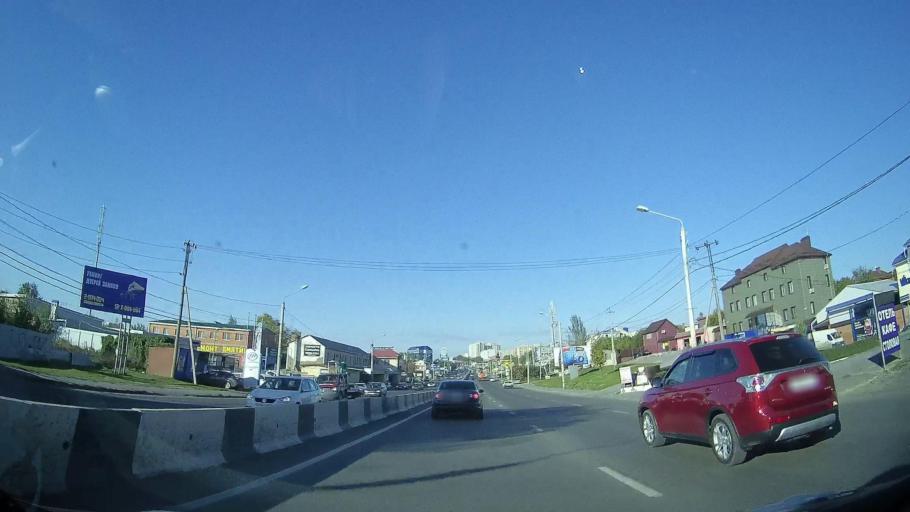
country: RU
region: Rostov
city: Kalinin
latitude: 47.2193
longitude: 39.6134
